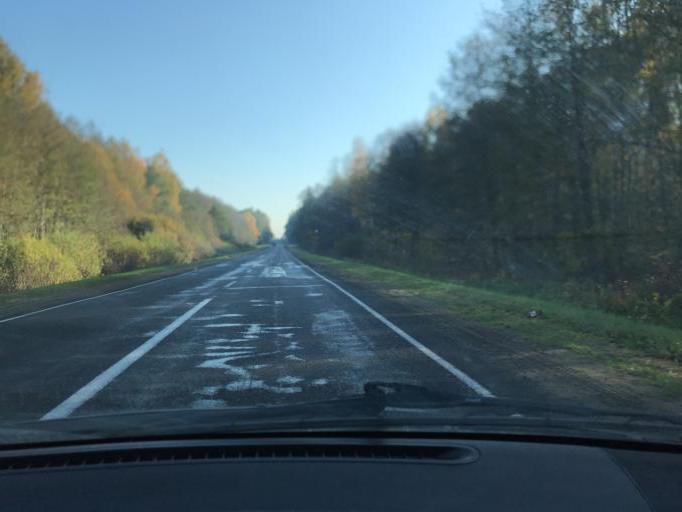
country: BY
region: Brest
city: Lyakhavichy
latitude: 52.9541
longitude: 26.2503
